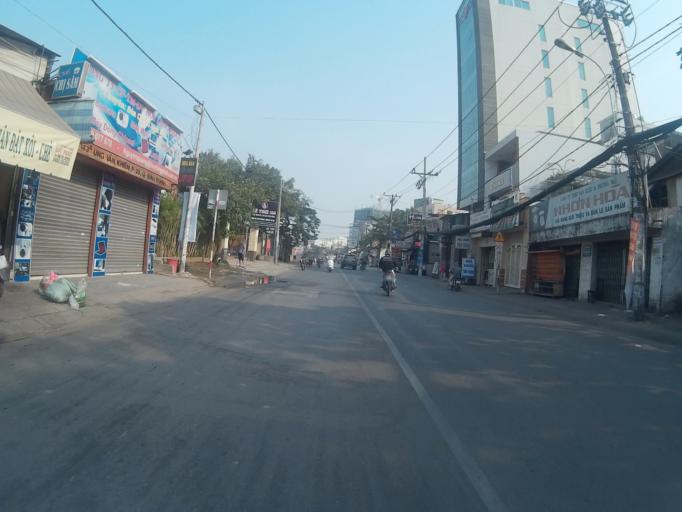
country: VN
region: Ho Chi Minh City
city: Quan Binh Thanh
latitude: 10.8093
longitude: 106.7138
